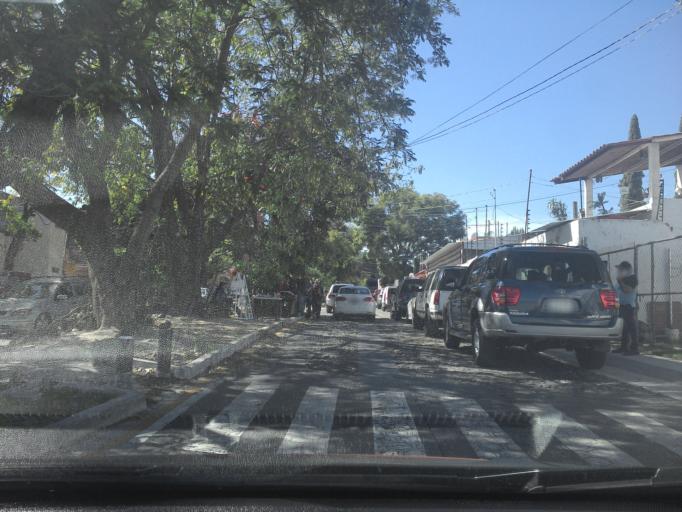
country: MX
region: Jalisco
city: Guadalajara
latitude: 20.6714
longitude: -103.4469
